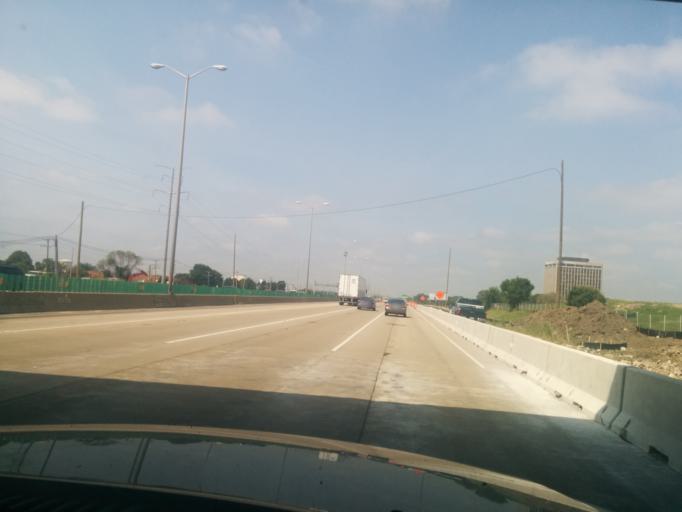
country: US
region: Illinois
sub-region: Cook County
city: Hoffman Estates
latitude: 42.0597
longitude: -88.0447
